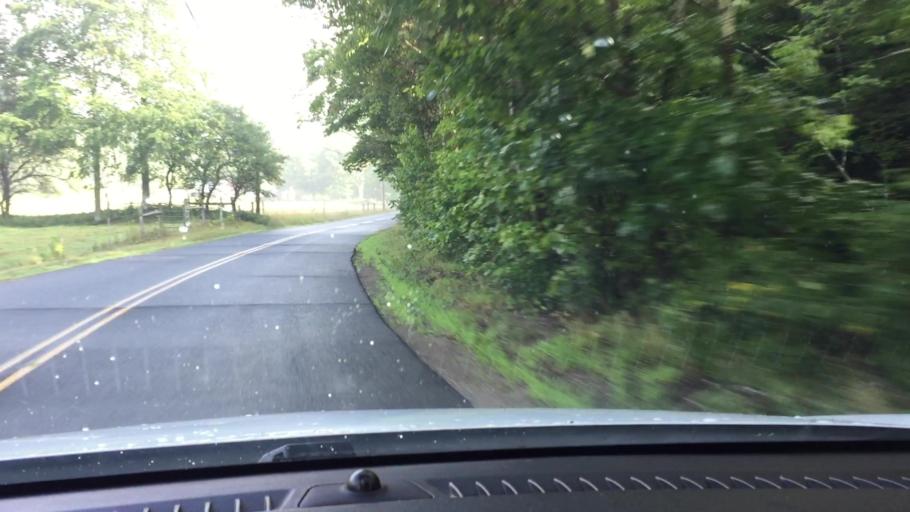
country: US
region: Massachusetts
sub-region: Berkshire County
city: Becket
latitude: 42.3952
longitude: -72.9791
